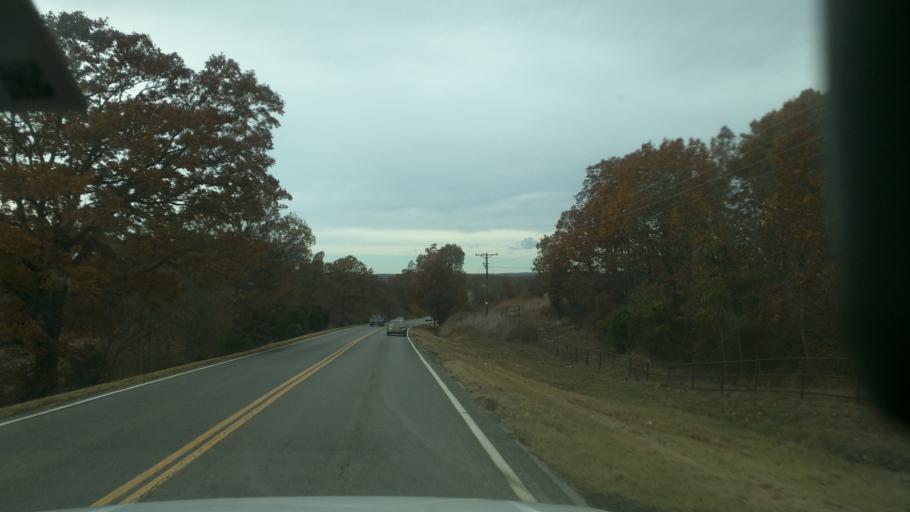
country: US
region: Oklahoma
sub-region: Cherokee County
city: Park Hill
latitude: 35.9032
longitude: -94.8230
